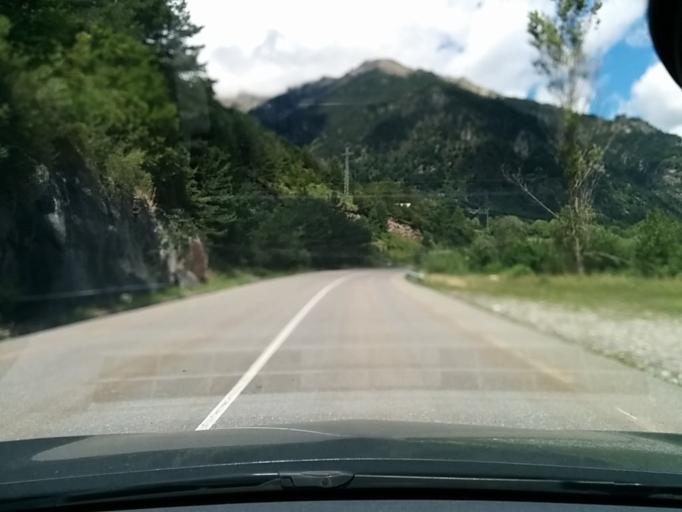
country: ES
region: Aragon
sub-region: Provincia de Huesca
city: Bielsa
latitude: 42.6518
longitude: 0.2084
